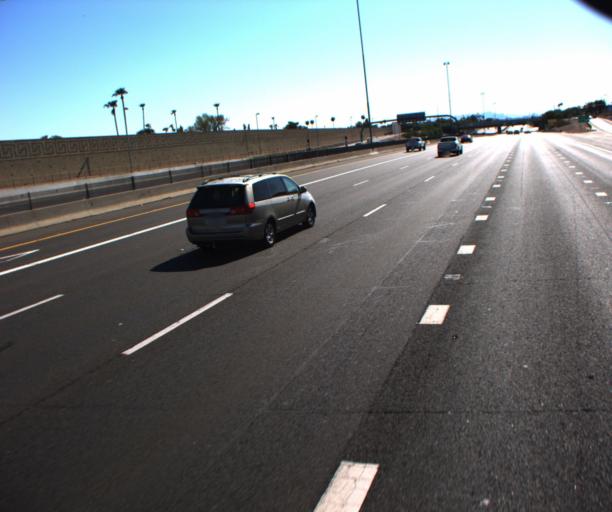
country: US
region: Arizona
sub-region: Maricopa County
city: Tempe
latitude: 33.3855
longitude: -111.9143
